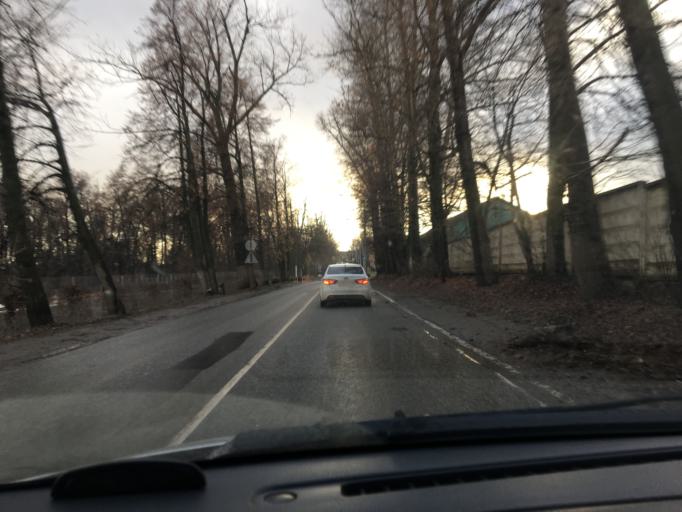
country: RU
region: Moscow
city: Zagor'ye
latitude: 55.5639
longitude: 37.6866
